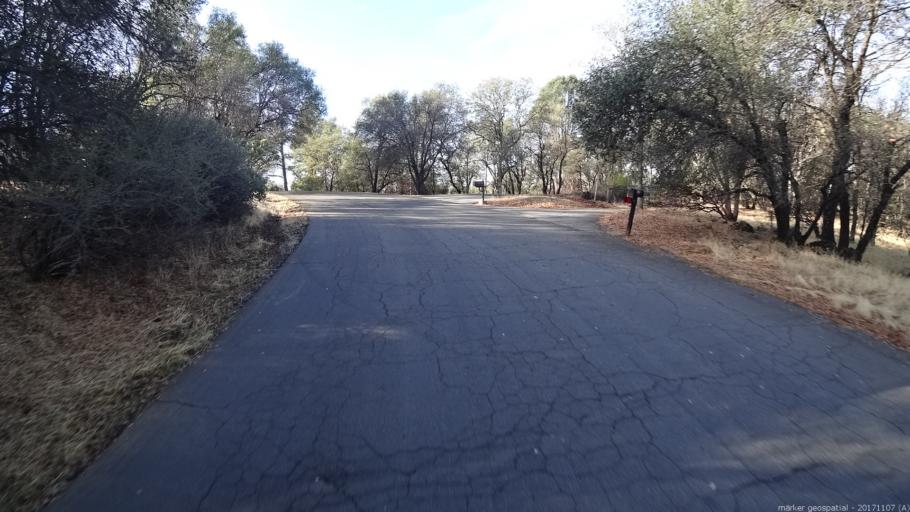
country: US
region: California
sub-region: Shasta County
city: Shasta
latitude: 40.5414
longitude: -122.4582
